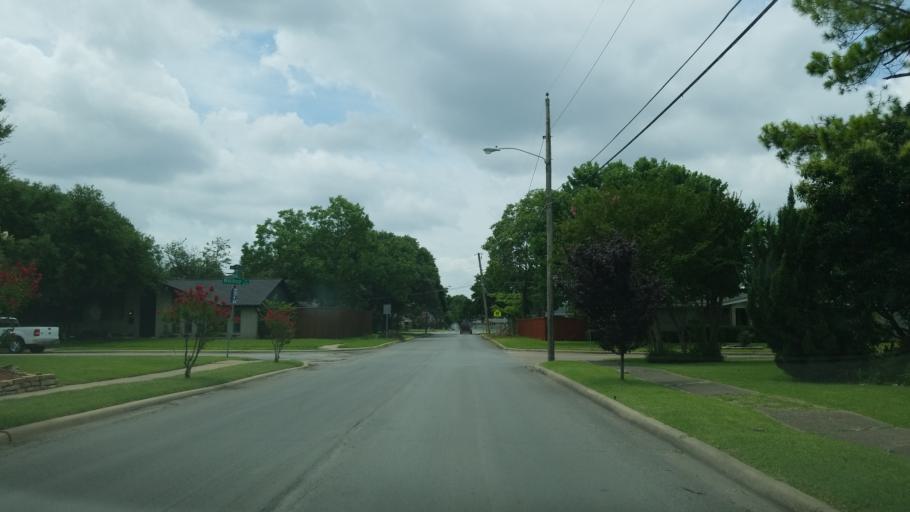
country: US
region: Texas
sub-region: Dallas County
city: Farmers Branch
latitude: 32.8907
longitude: -96.8730
